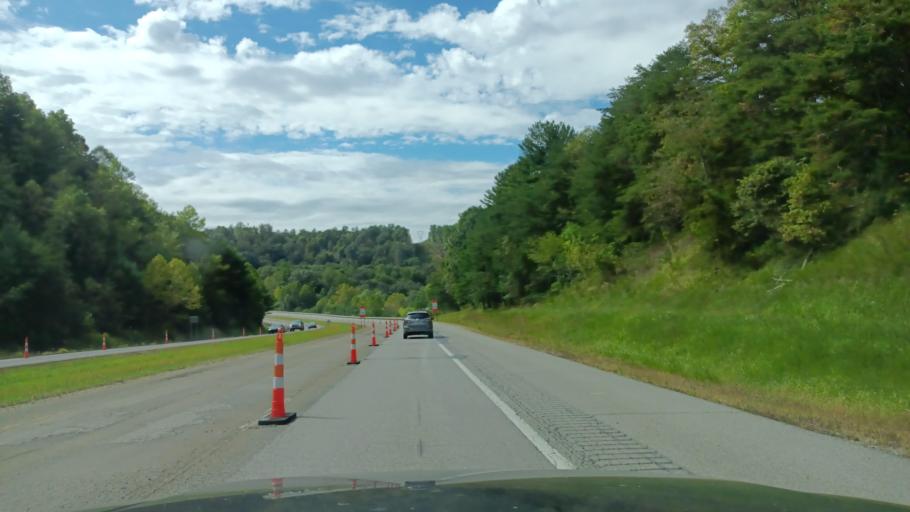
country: US
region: West Virginia
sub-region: Ritchie County
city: Harrisville
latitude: 39.2612
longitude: -81.0993
